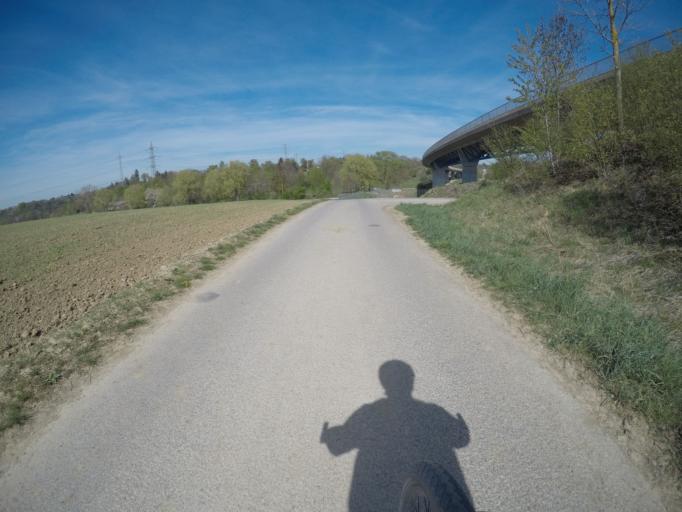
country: DE
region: Baden-Wuerttemberg
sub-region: Regierungsbezirk Stuttgart
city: Schwieberdingen
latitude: 48.8595
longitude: 9.0845
